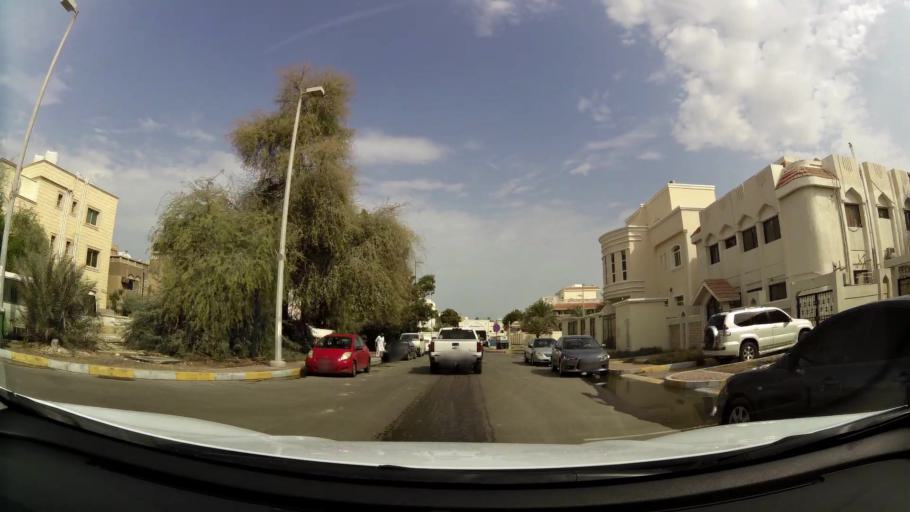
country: AE
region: Abu Dhabi
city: Abu Dhabi
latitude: 24.4404
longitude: 54.4299
